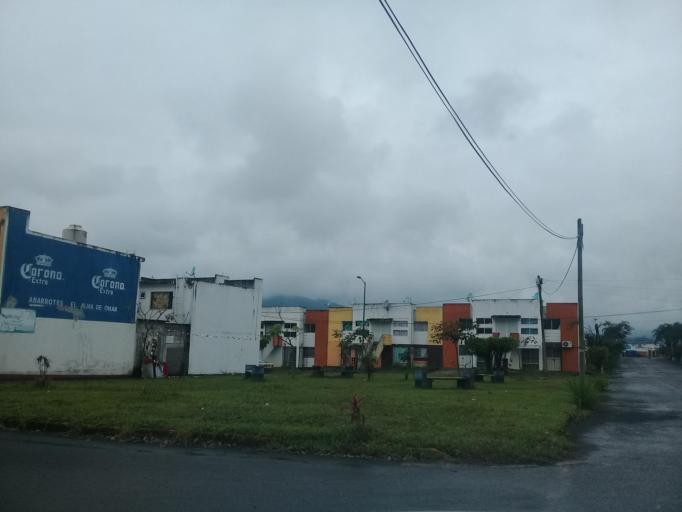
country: MX
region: Veracruz
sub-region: Amatlan de los Reyes
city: Trapiche Viejo
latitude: 18.8379
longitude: -96.9507
